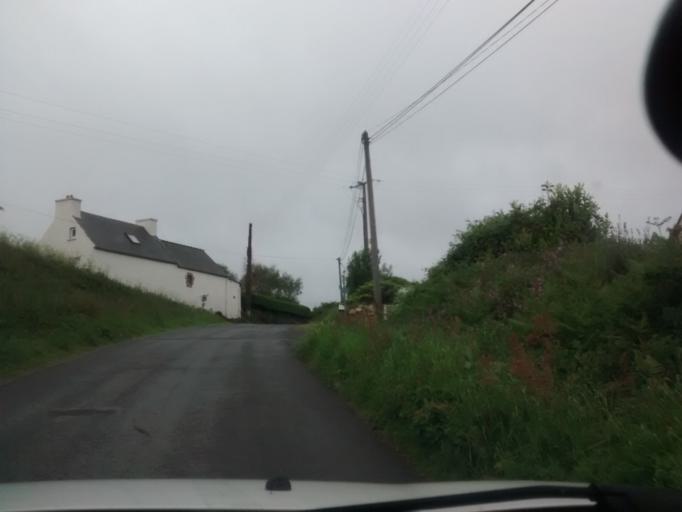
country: FR
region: Brittany
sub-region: Departement des Cotes-d'Armor
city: Plougrescant
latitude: 48.8467
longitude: -3.2177
